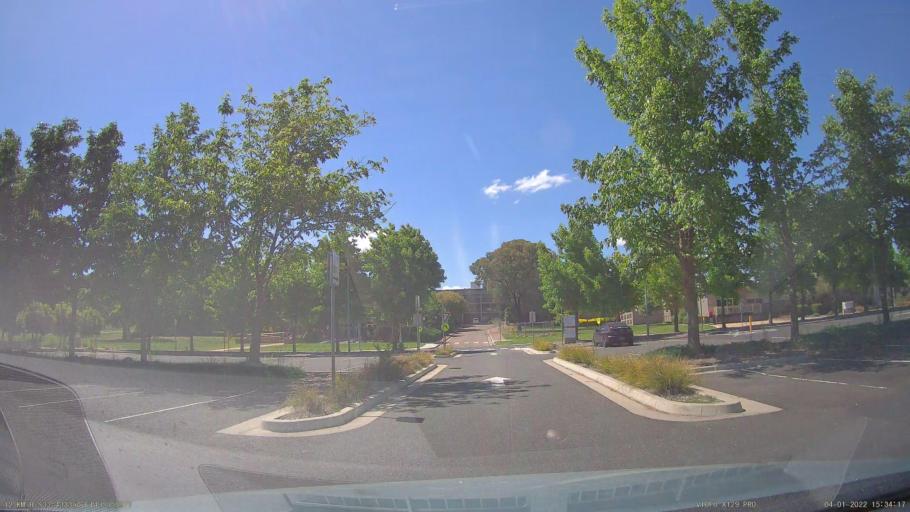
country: AU
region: New South Wales
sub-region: Bathurst Regional
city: Bathurst
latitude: -33.4334
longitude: 149.5600
